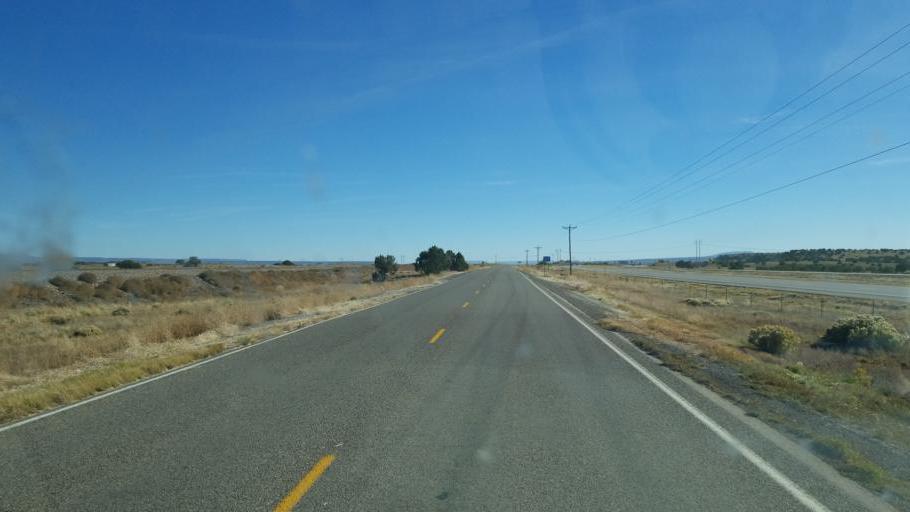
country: US
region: New Mexico
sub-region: Cibola County
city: Milan
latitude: 35.3197
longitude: -107.9946
